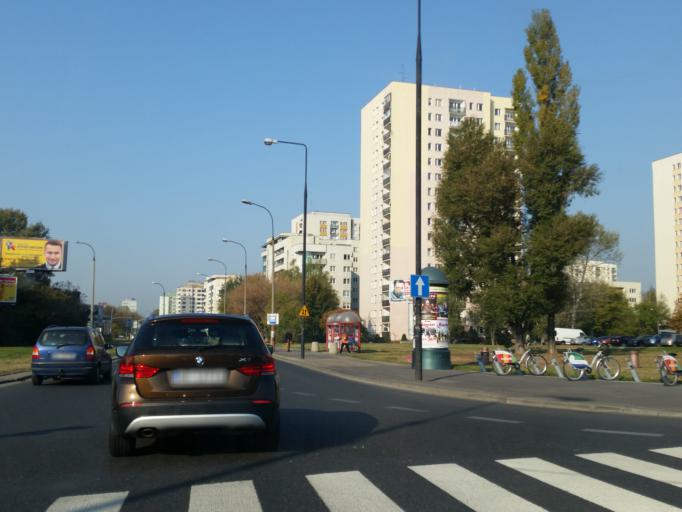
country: PL
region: Masovian Voivodeship
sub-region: Warszawa
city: Mokotow
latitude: 52.1800
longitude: 21.0210
